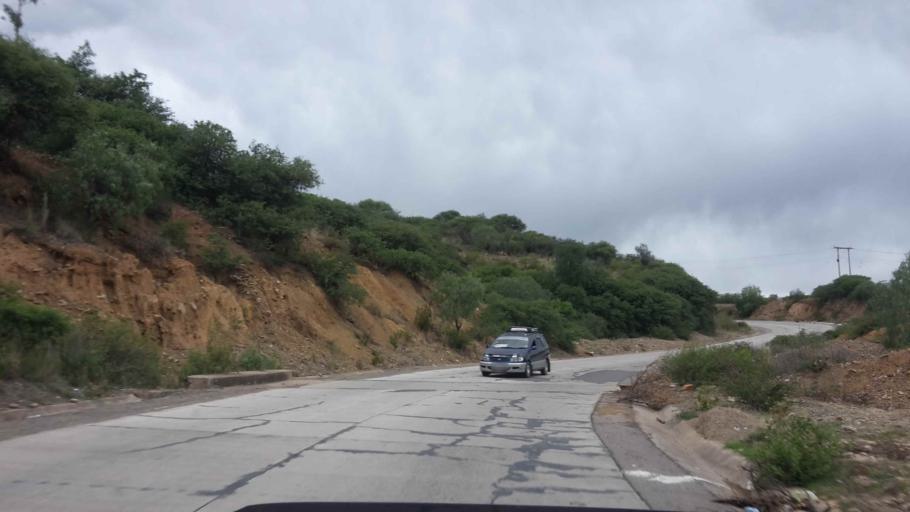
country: BO
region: Cochabamba
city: Cochabamba
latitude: -17.5307
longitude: -66.1999
